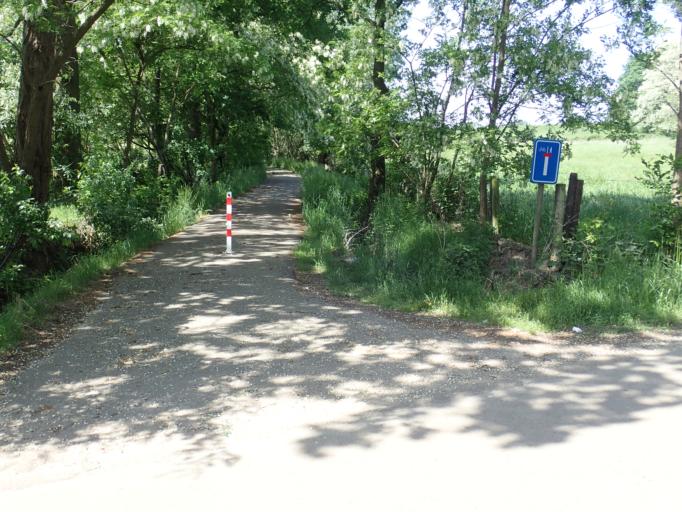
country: BE
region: Flanders
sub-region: Provincie Antwerpen
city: Herselt
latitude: 51.0679
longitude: 4.9007
